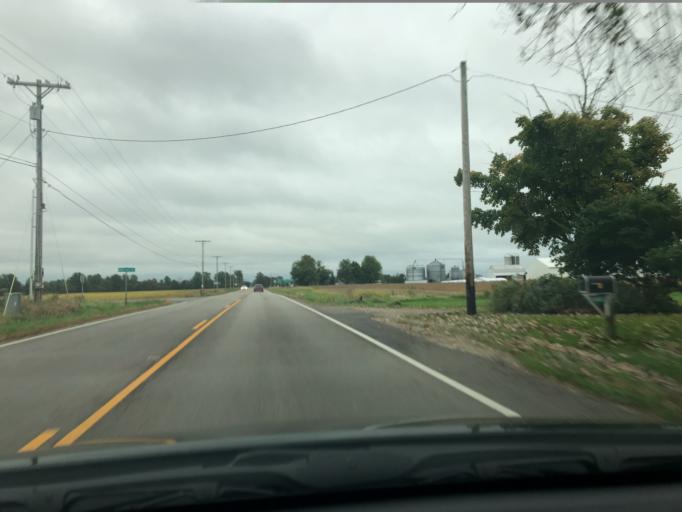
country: US
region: Ohio
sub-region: Union County
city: New California
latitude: 40.2637
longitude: -83.2509
